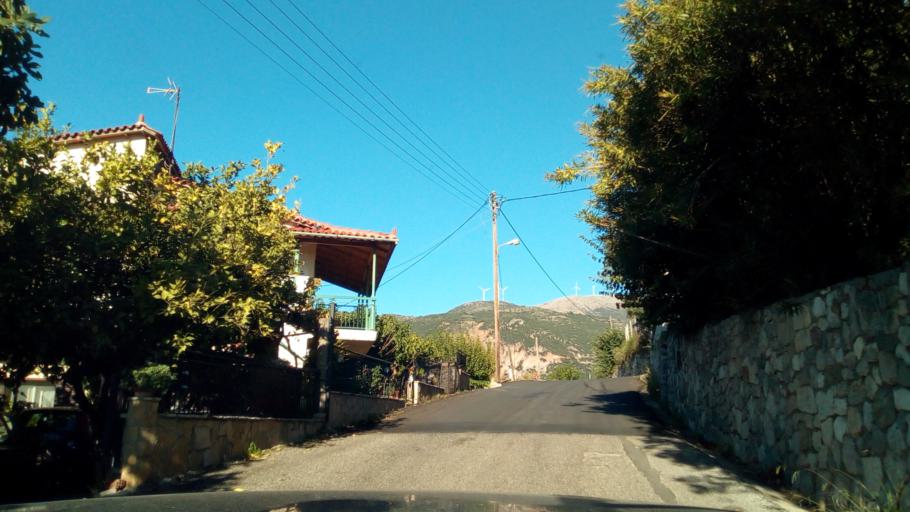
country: GR
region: West Greece
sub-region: Nomos Aitolias kai Akarnanias
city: Nafpaktos
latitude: 38.4215
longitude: 21.8435
